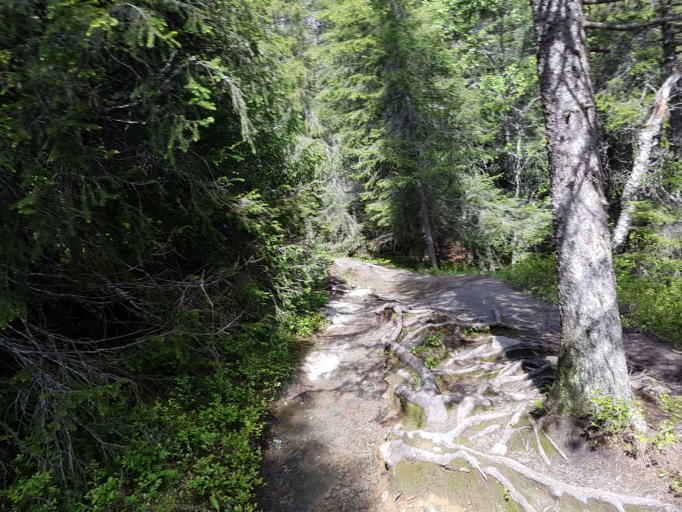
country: NO
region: Sor-Trondelag
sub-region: Trondheim
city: Trondheim
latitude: 63.4282
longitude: 10.3057
